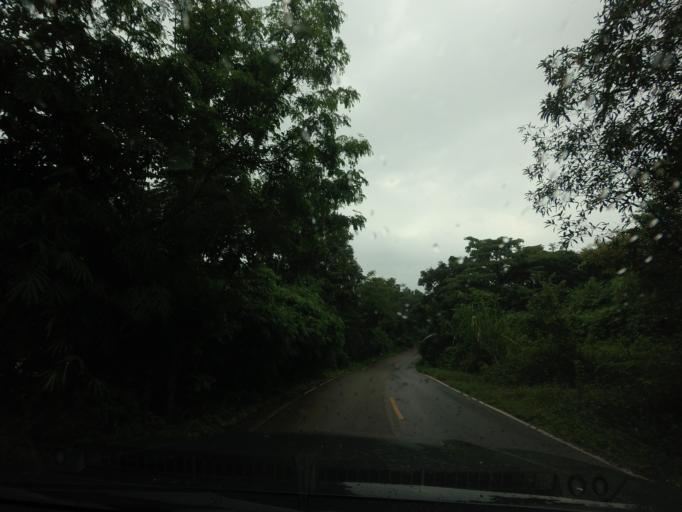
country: TH
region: Nong Khai
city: Sangkhom
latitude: 18.0374
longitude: 102.3126
